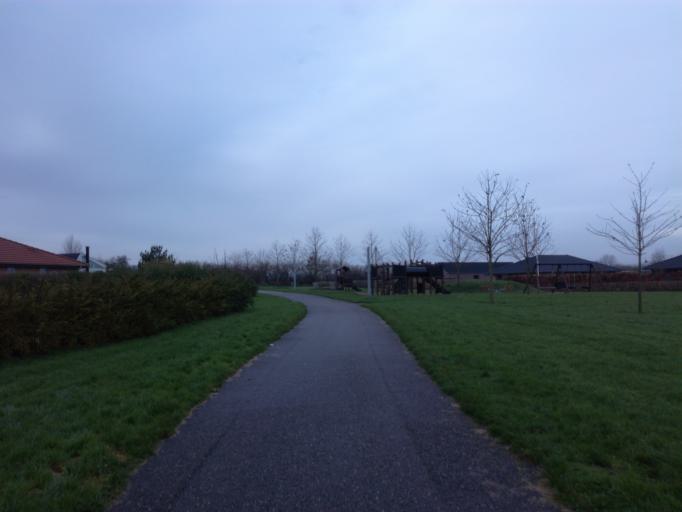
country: DK
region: South Denmark
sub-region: Vejle Kommune
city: Borkop
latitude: 55.6320
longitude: 9.6532
